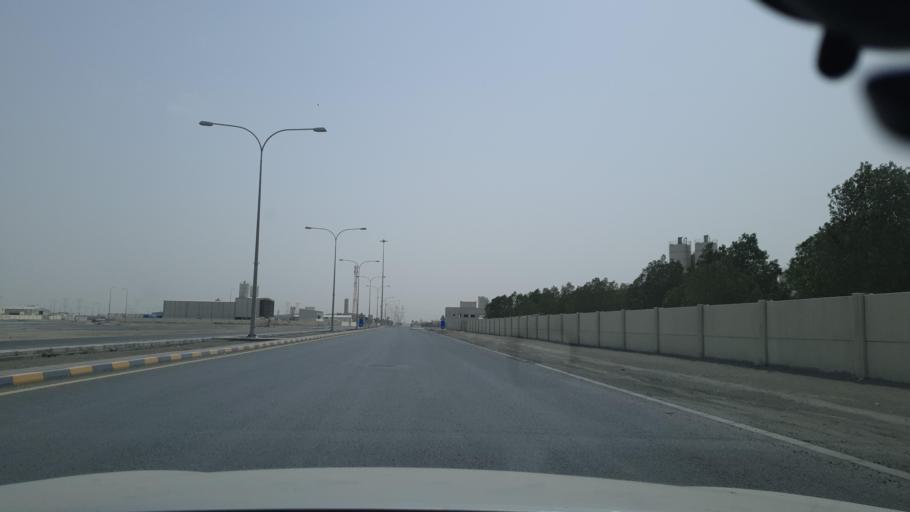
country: QA
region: Al Wakrah
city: Umm Sa'id
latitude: 25.0025
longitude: 51.5834
